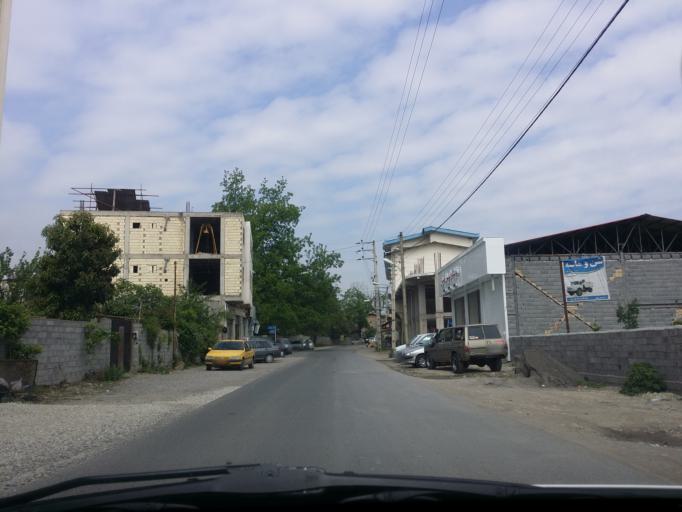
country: IR
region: Mazandaran
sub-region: Nowshahr
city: Nowshahr
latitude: 36.6268
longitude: 51.4868
